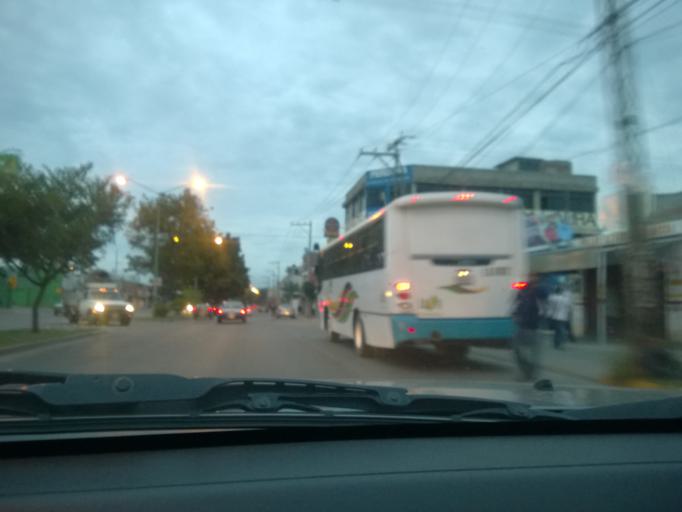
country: MX
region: Guanajuato
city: Leon
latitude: 21.1324
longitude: -101.6702
